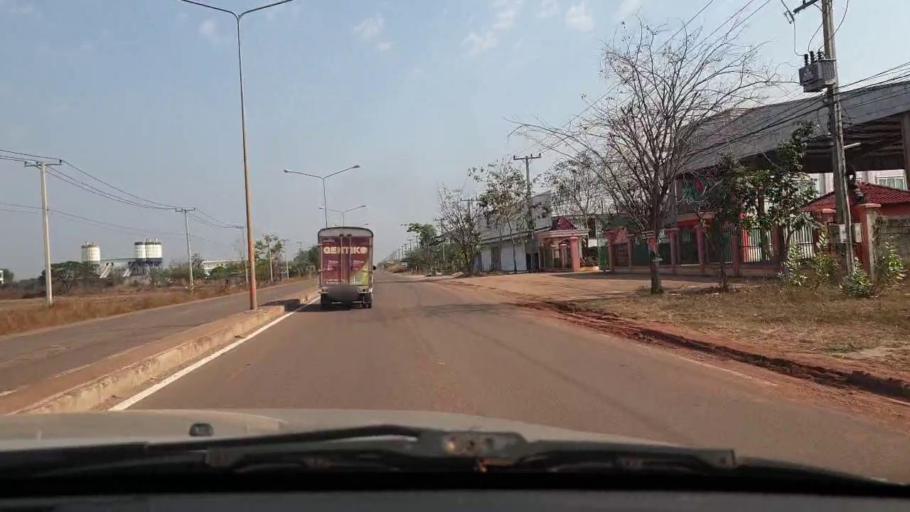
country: LA
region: Vientiane
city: Vientiane
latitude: 18.0121
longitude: 102.7225
